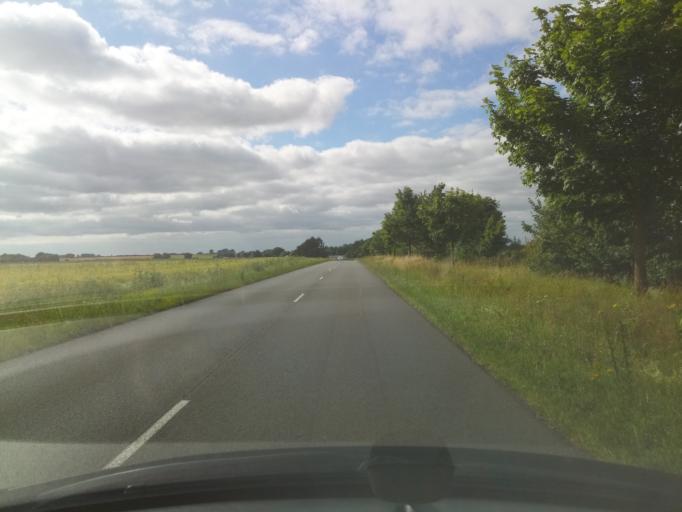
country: FR
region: Poitou-Charentes
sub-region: Departement de la Charente-Maritime
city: Surgeres
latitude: 46.1363
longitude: -0.7933
